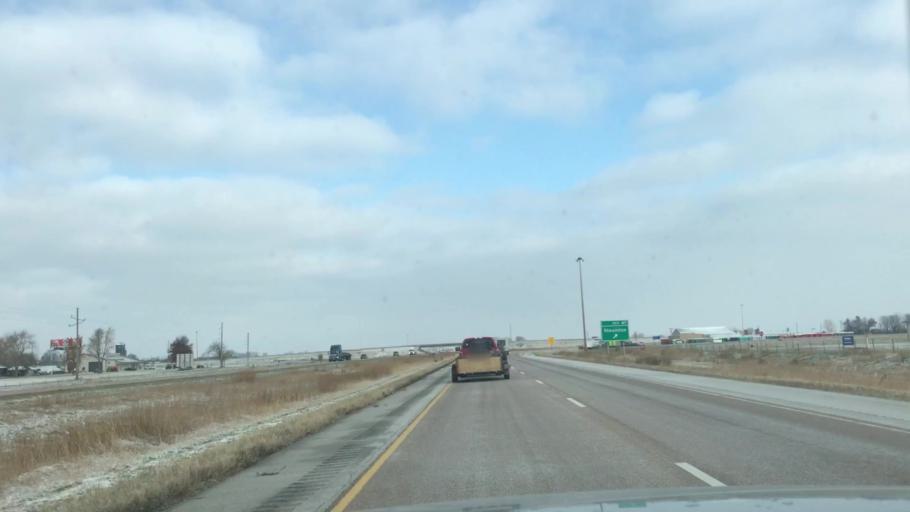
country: US
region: Illinois
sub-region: Macoupin County
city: Staunton
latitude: 39.0145
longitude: -89.7494
